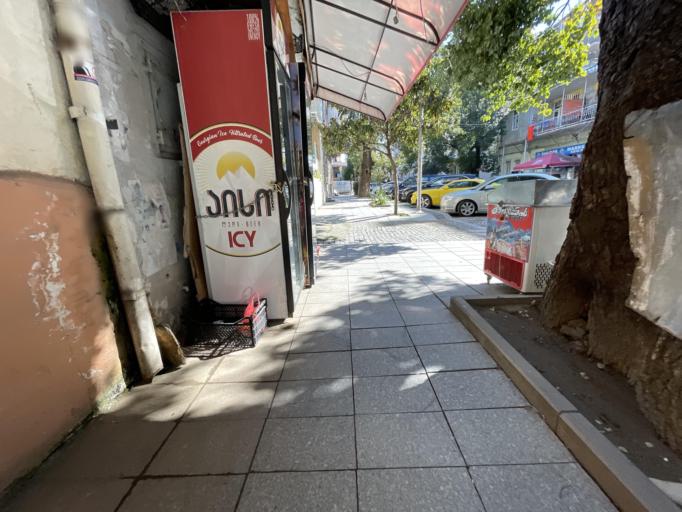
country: GE
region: Ajaria
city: Batumi
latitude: 41.6501
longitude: 41.6316
